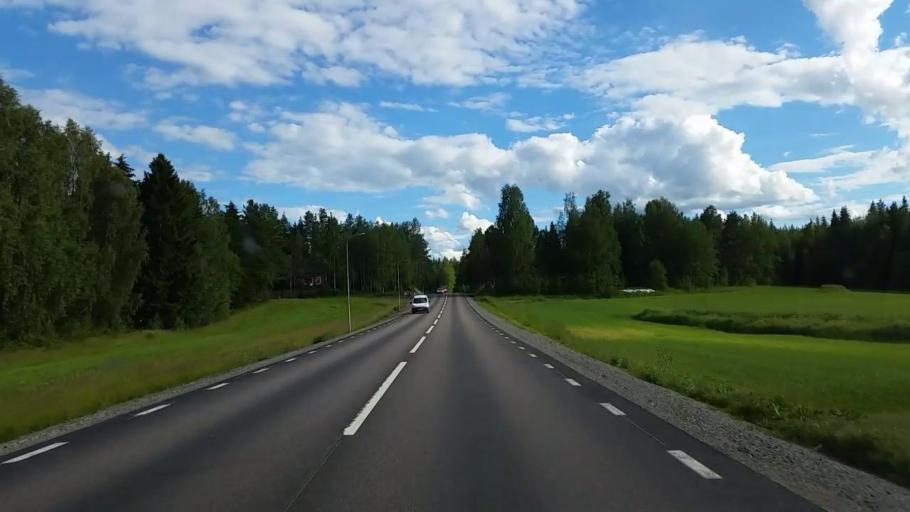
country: SE
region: Gaevleborg
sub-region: Ljusdals Kommun
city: Farila
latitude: 61.9274
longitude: 15.8735
